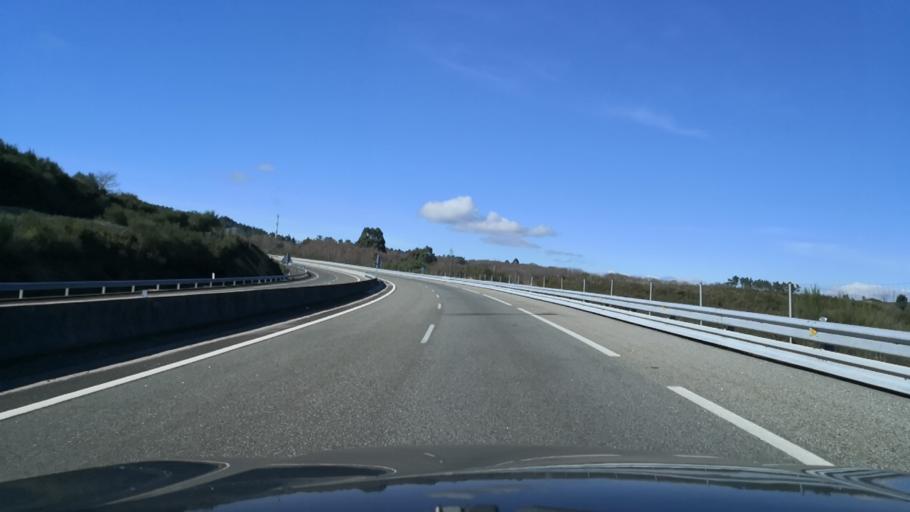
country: ES
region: Galicia
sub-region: Provincia de Pontevedra
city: Dozon
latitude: 42.5545
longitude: -8.0198
